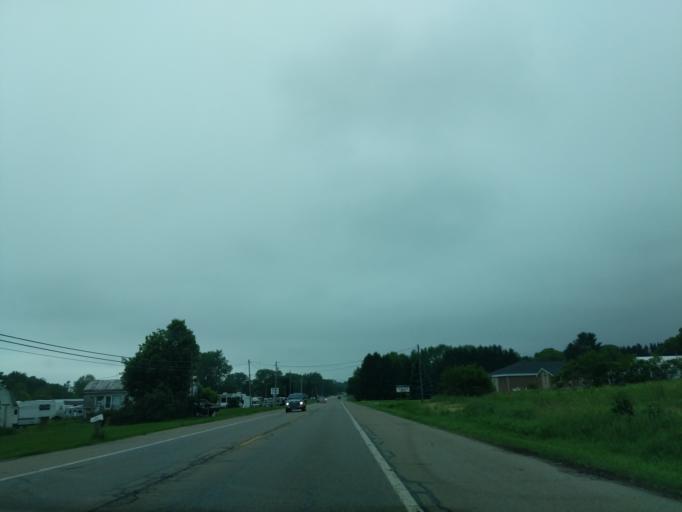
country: US
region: Michigan
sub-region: Branch County
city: Quincy
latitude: 41.9393
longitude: -84.9261
